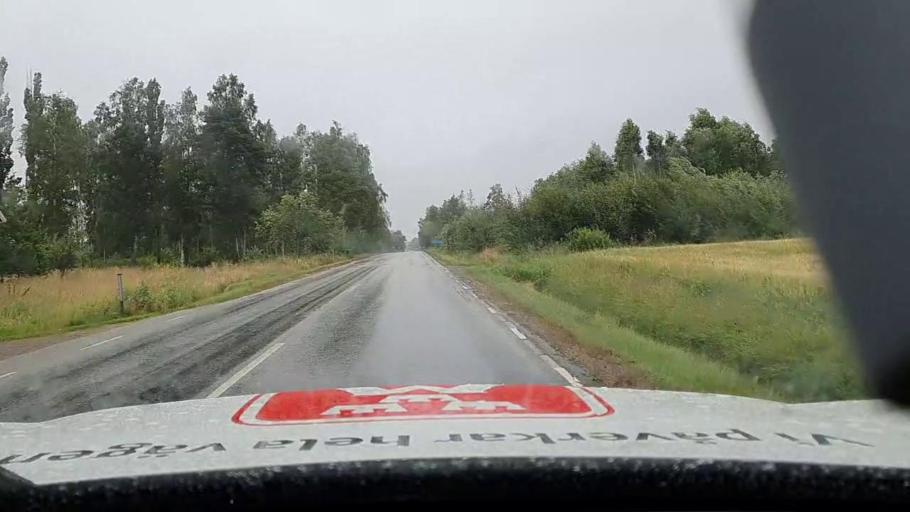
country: SE
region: Vaestra Goetaland
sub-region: Toreboda Kommun
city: Toereboda
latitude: 58.7004
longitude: 14.1346
